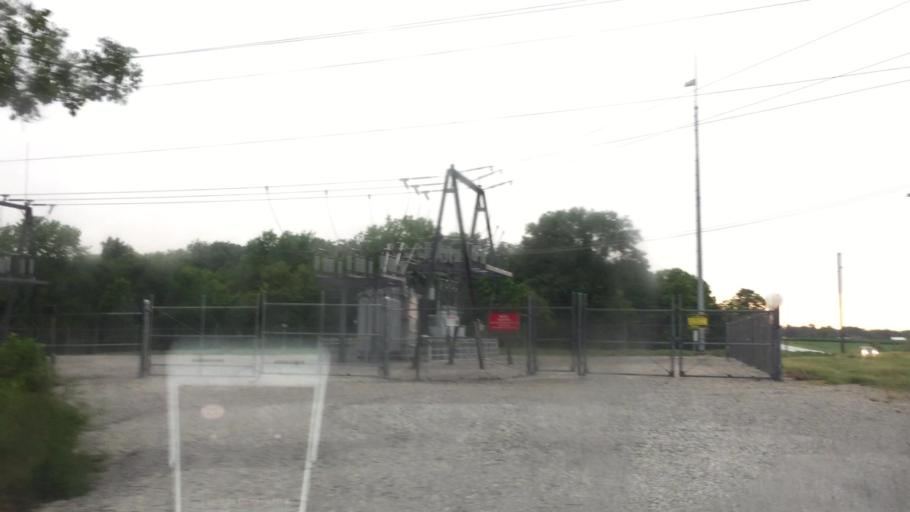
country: US
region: Illinois
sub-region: Hancock County
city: Nauvoo
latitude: 40.5519
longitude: -91.3513
